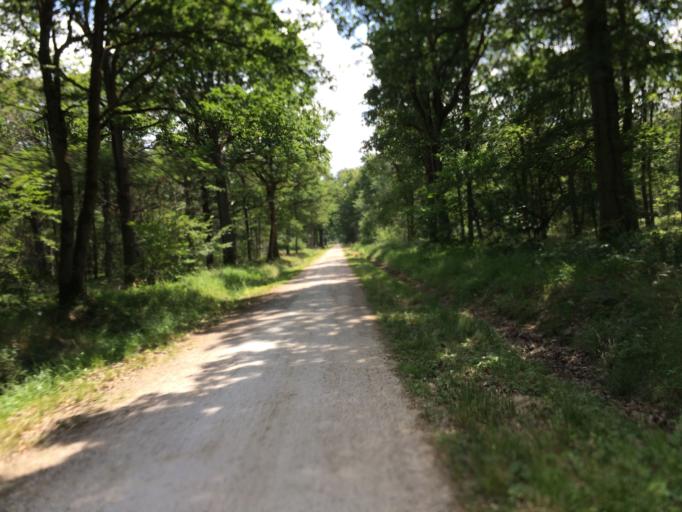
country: FR
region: Ile-de-France
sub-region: Departement de l'Essonne
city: Brunoy
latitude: 48.6724
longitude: 2.4952
